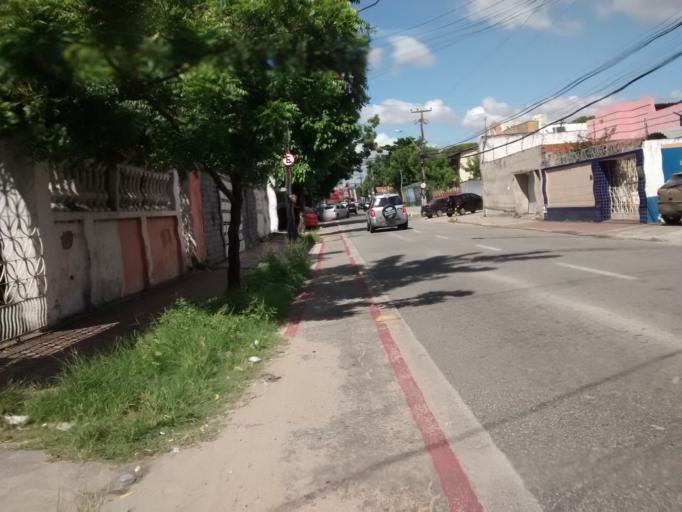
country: BR
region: Ceara
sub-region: Fortaleza
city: Fortaleza
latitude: -3.7312
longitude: -38.5520
